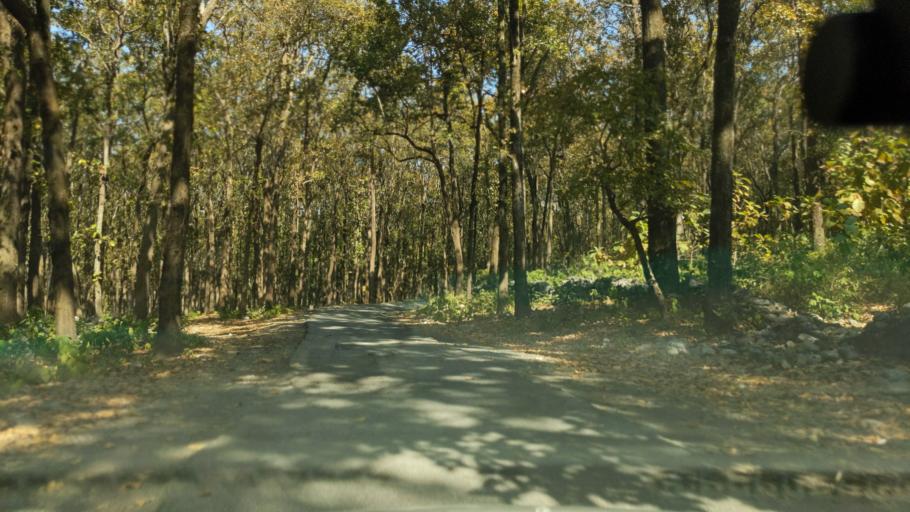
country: IN
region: Uttarakhand
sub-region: Naini Tal
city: Ramnagar
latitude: 29.4668
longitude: 79.2329
